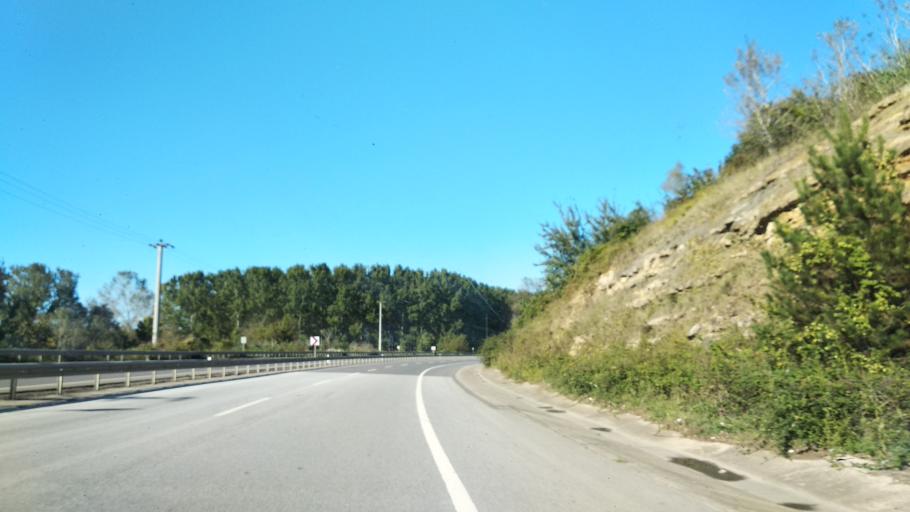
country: TR
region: Sakarya
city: Karasu
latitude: 41.0871
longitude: 30.6471
